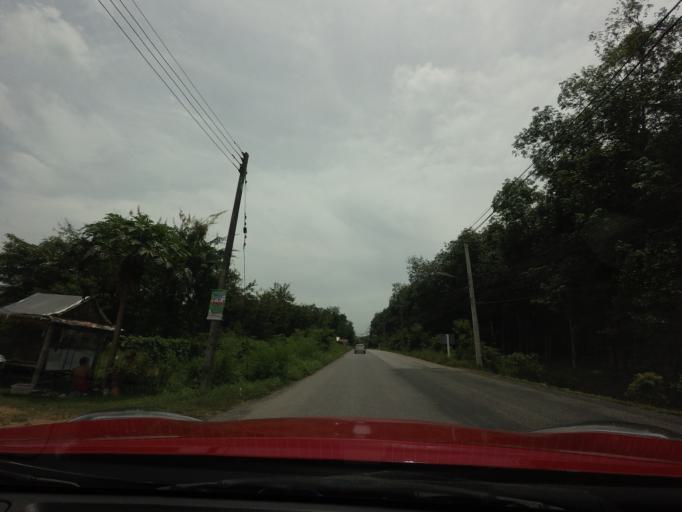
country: TH
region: Songkhla
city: Hat Yai
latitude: 7.0021
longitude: 100.5283
